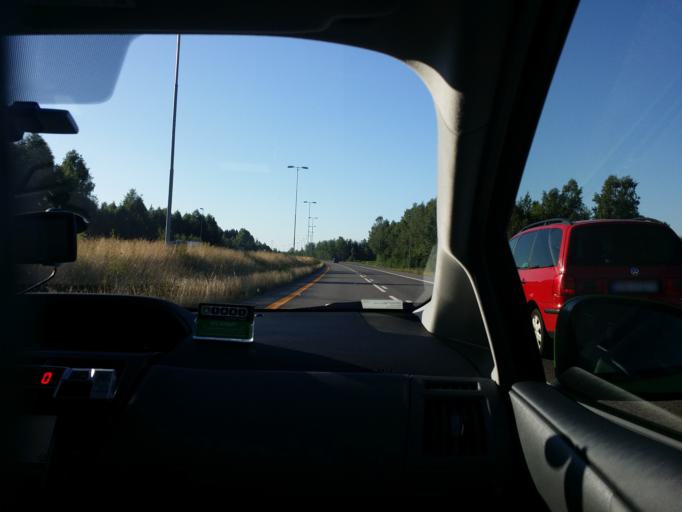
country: NO
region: Akershus
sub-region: Ullensaker
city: Jessheim
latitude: 60.1775
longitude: 11.0954
